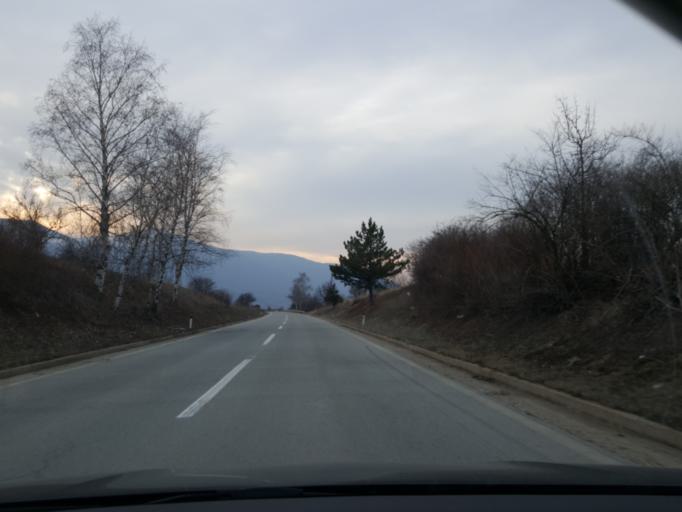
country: RS
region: Central Serbia
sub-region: Pirotski Okrug
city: Bela Palanka
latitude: 43.2224
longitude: 22.3560
